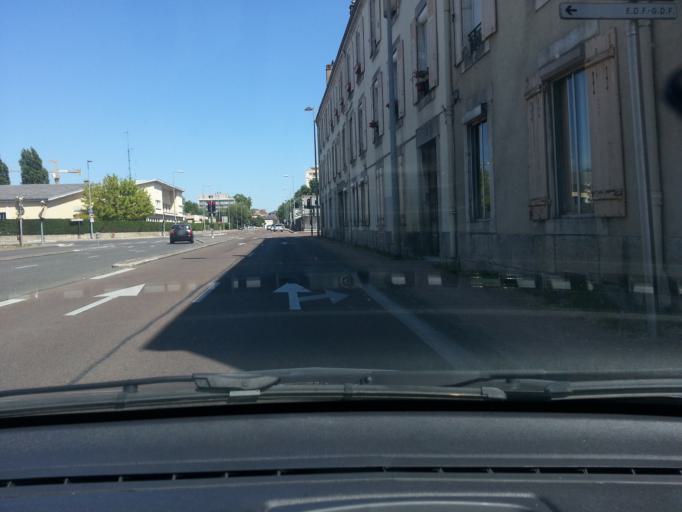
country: FR
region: Bourgogne
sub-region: Departement de la Cote-d'Or
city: Dijon
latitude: 47.3086
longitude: 5.0329
